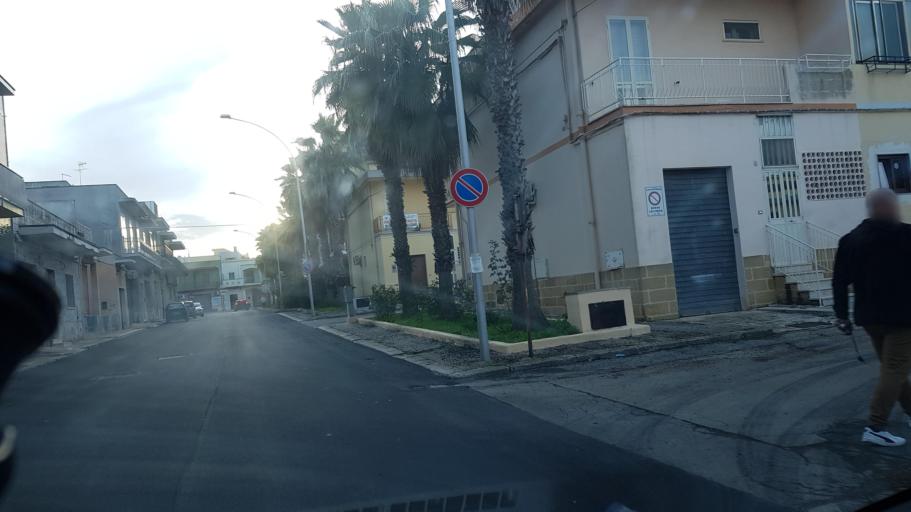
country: IT
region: Apulia
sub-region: Provincia di Brindisi
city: San Vito dei Normanni
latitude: 40.6616
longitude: 17.7050
